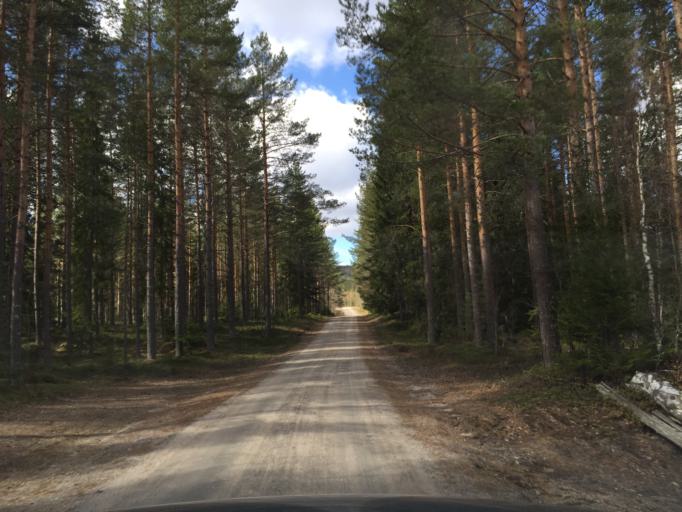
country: SE
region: Gaevleborg
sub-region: Bollnas Kommun
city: Arbra
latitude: 61.5219
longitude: 16.2997
